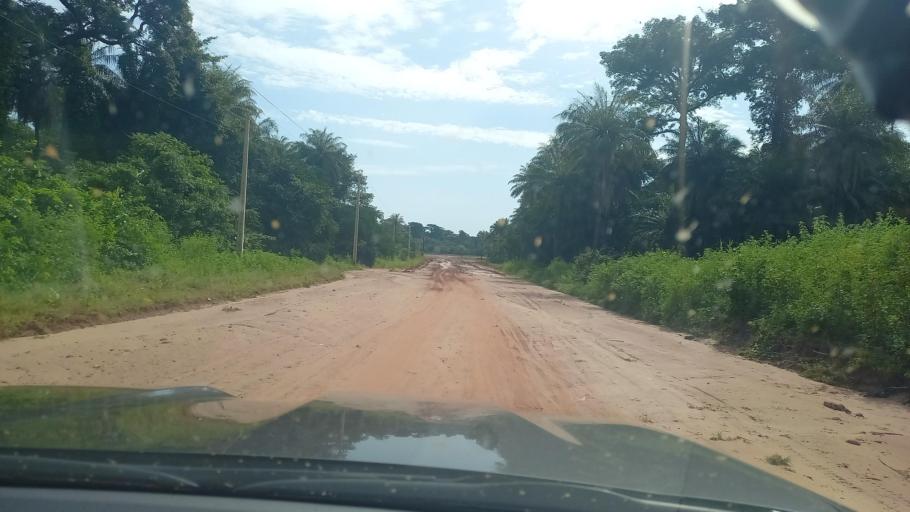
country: SN
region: Ziguinchor
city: Ziguinchor
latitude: 12.6734
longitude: -16.2068
